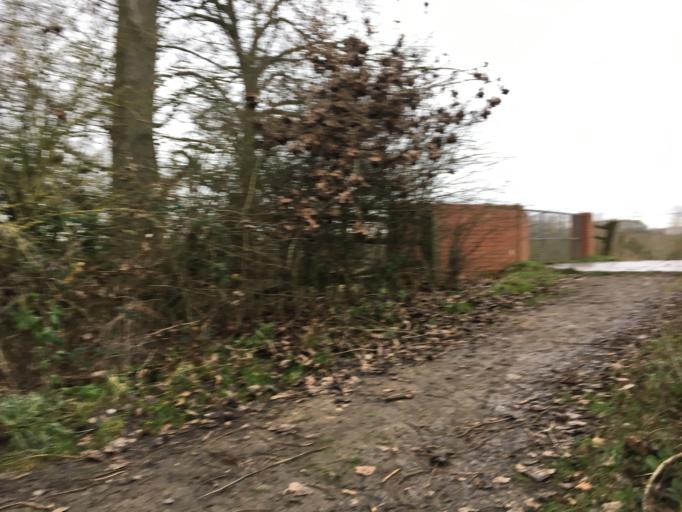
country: GB
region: England
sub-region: Warwickshire
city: Rugby
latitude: 52.4007
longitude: -1.2593
